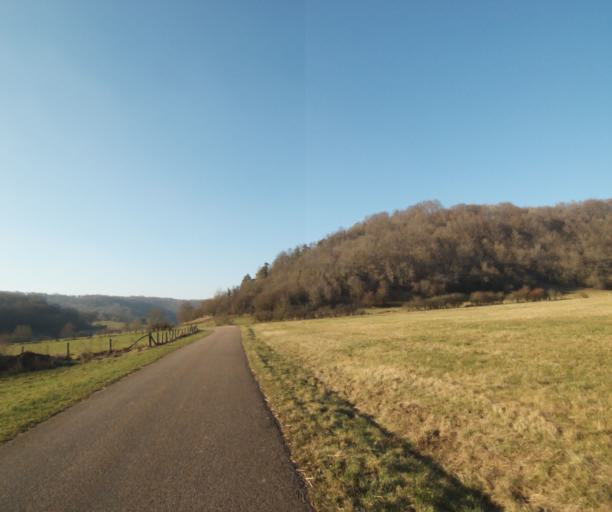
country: FR
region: Champagne-Ardenne
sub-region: Departement de la Haute-Marne
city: Joinville
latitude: 48.4893
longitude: 5.2036
